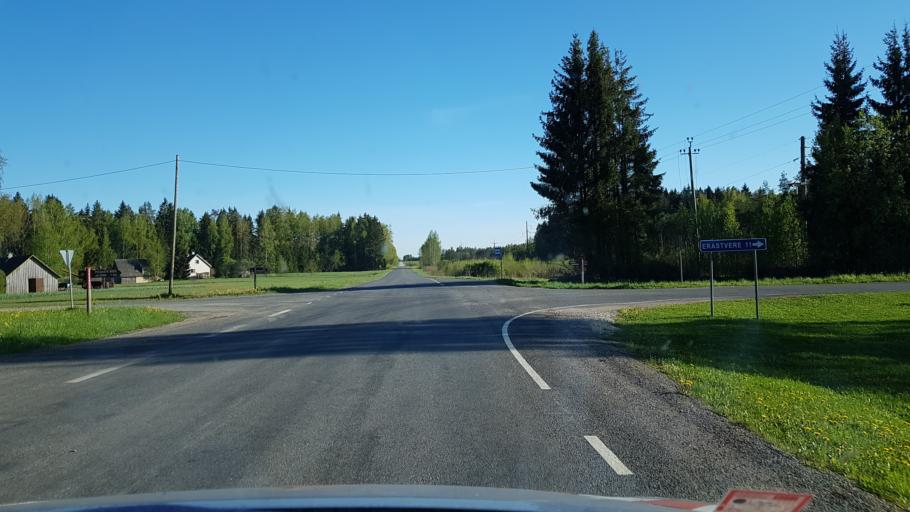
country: EE
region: Vorumaa
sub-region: Voru linn
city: Voru
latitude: 57.9426
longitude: 26.9536
